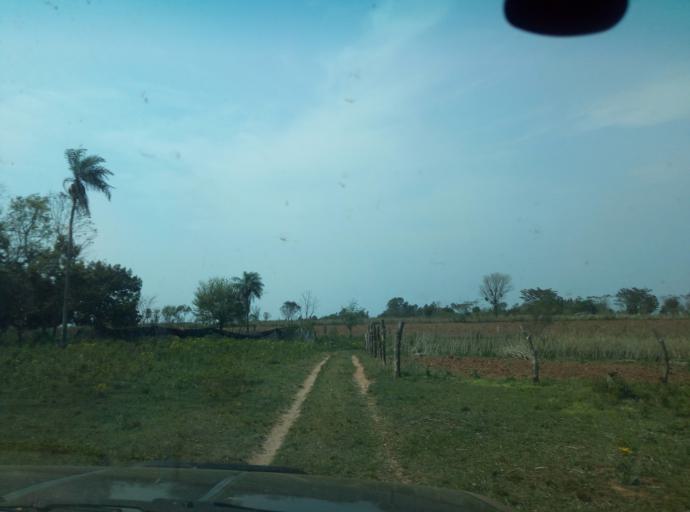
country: PY
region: Caaguazu
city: San Joaquin
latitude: -25.1427
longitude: -56.1004
